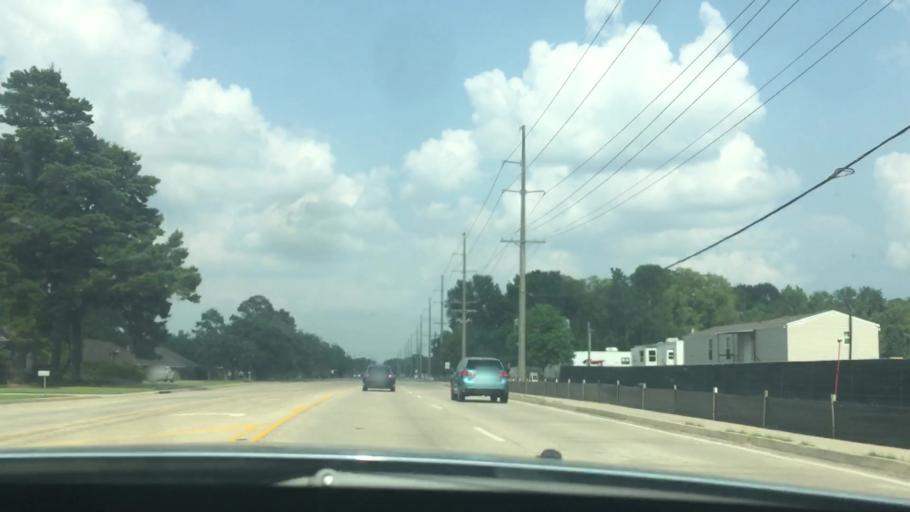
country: US
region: Louisiana
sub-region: East Baton Rouge Parish
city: Westminster
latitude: 30.4374
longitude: -91.0551
